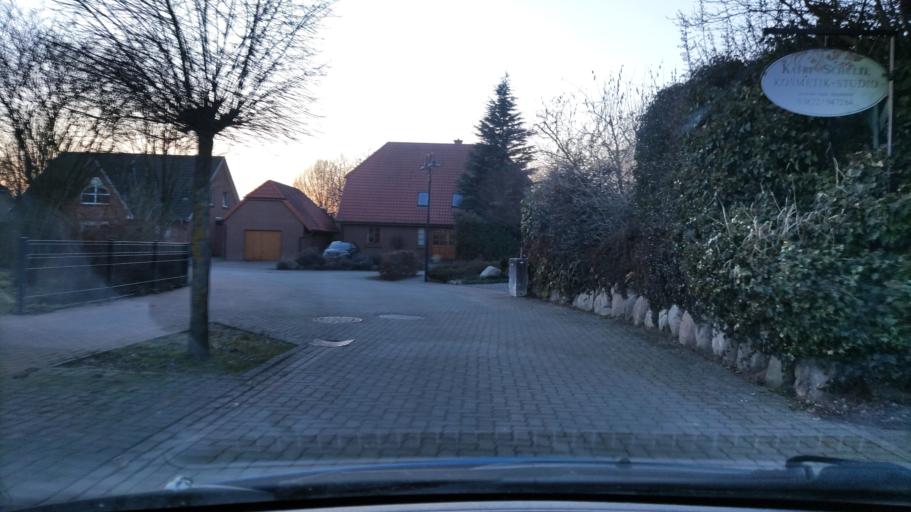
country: DE
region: Lower Saxony
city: Ebstorf
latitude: 53.0243
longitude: 10.4275
